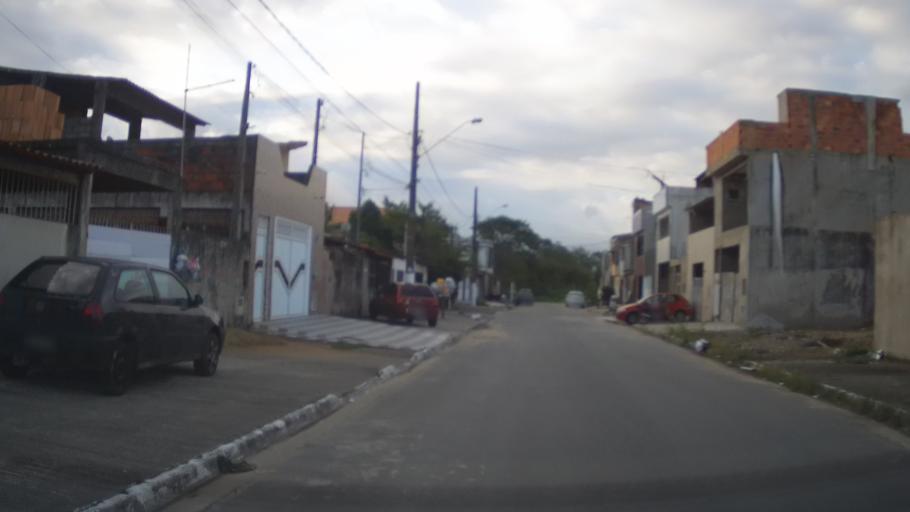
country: BR
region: Sao Paulo
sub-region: Praia Grande
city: Praia Grande
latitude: -23.9959
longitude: -46.4284
